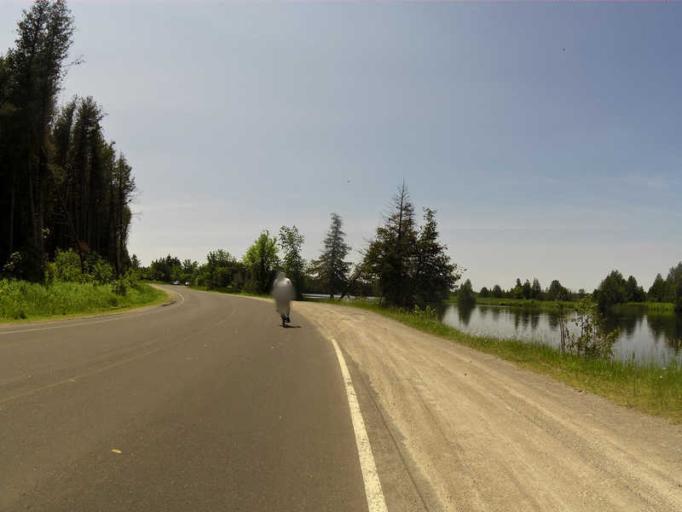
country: CA
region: Ontario
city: Peterborough
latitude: 44.3942
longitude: -78.2655
